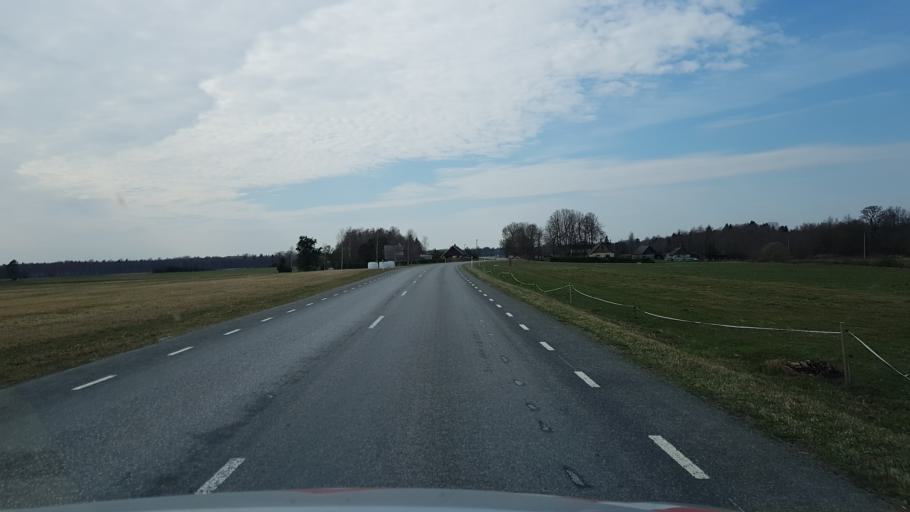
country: EE
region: Laeaene-Virumaa
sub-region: Haljala vald
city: Haljala
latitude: 59.4595
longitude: 26.2126
